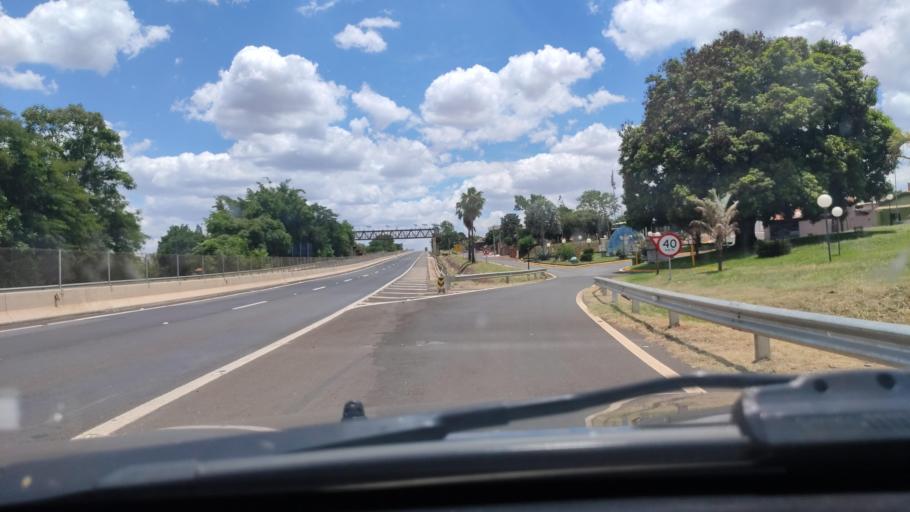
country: BR
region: Sao Paulo
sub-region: Duartina
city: Duartina
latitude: -22.6966
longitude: -49.4283
